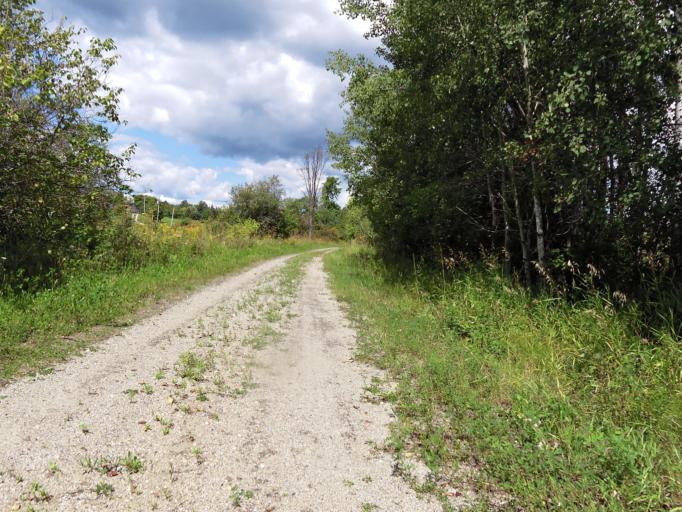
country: CA
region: Quebec
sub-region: Outaouais
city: Wakefield
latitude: 45.8311
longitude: -75.9795
